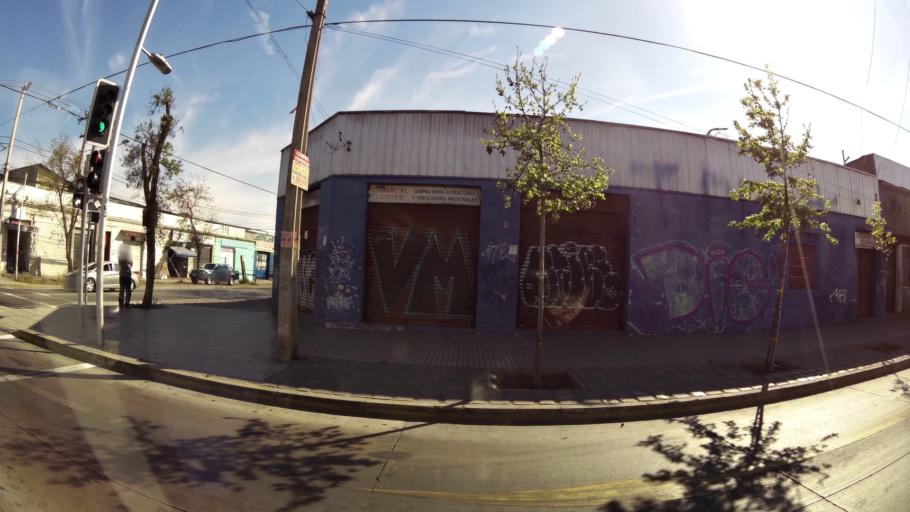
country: CL
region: Santiago Metropolitan
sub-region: Provincia de Santiago
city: Santiago
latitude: -33.4685
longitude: -70.6367
